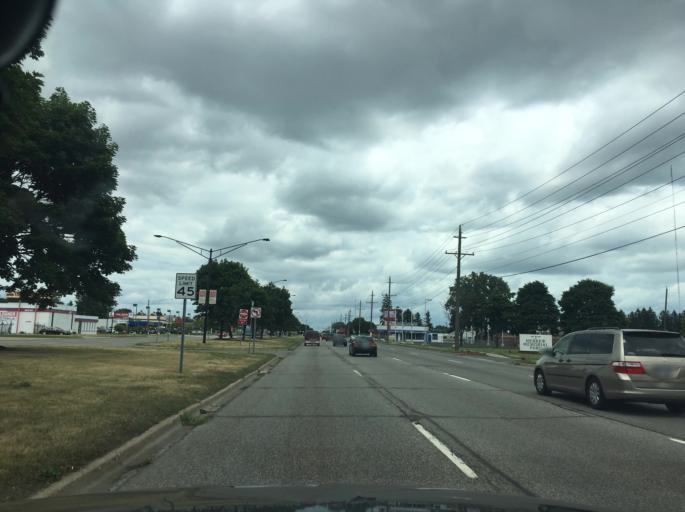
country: US
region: Michigan
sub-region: Macomb County
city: Fraser
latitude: 42.5413
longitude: -82.9078
